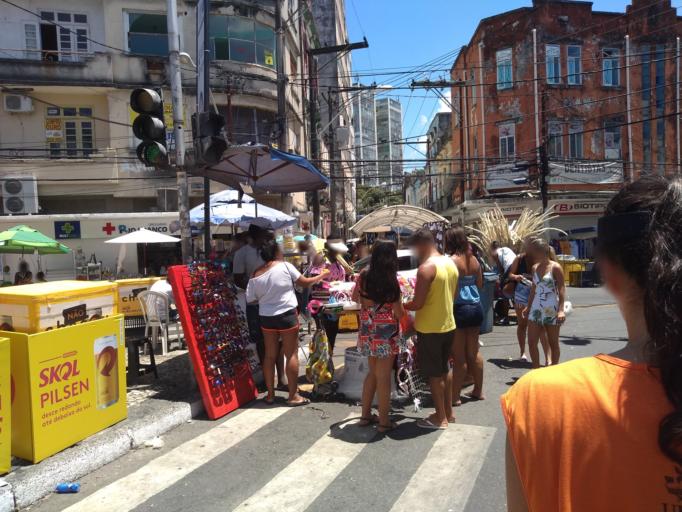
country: BR
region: Bahia
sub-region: Salvador
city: Salvador
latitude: -12.9825
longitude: -38.5142
